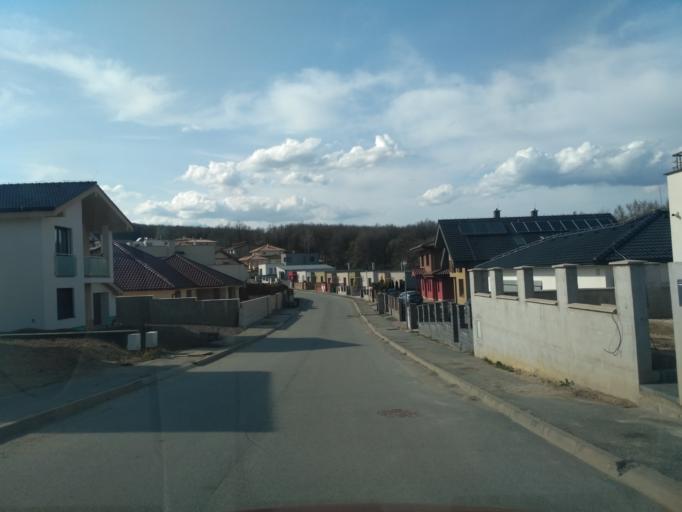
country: SK
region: Kosicky
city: Kosice
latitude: 48.6941
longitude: 21.2004
